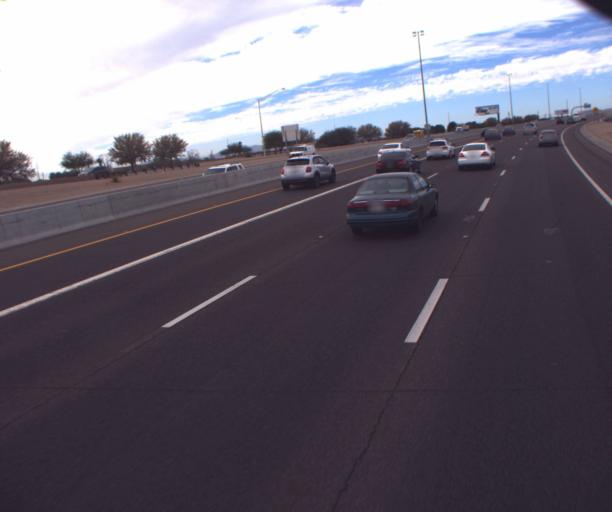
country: US
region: Arizona
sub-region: Maricopa County
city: Chandler
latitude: 33.2828
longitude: -111.8260
